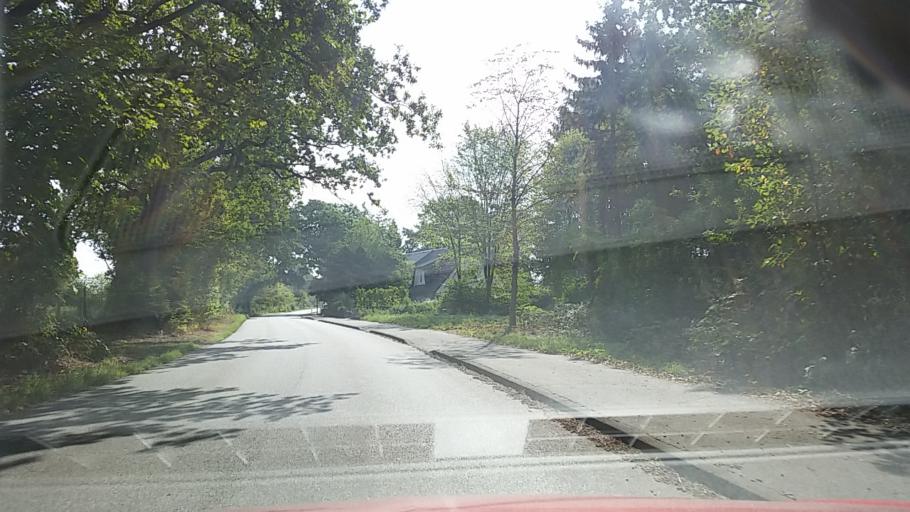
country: DE
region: Schleswig-Holstein
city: Pinneberg
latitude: 53.6319
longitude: 9.7699
